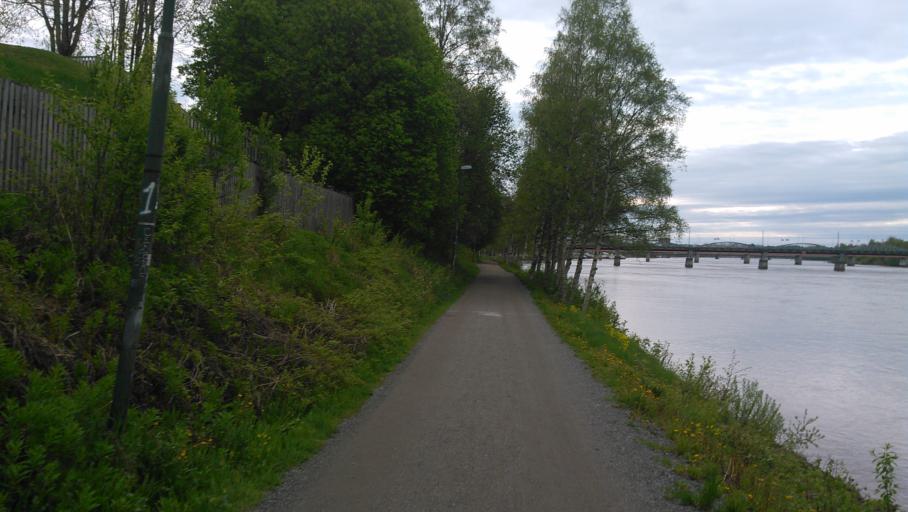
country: SE
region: Vaesterbotten
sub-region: Umea Kommun
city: Umea
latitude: 63.8269
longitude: 20.2425
